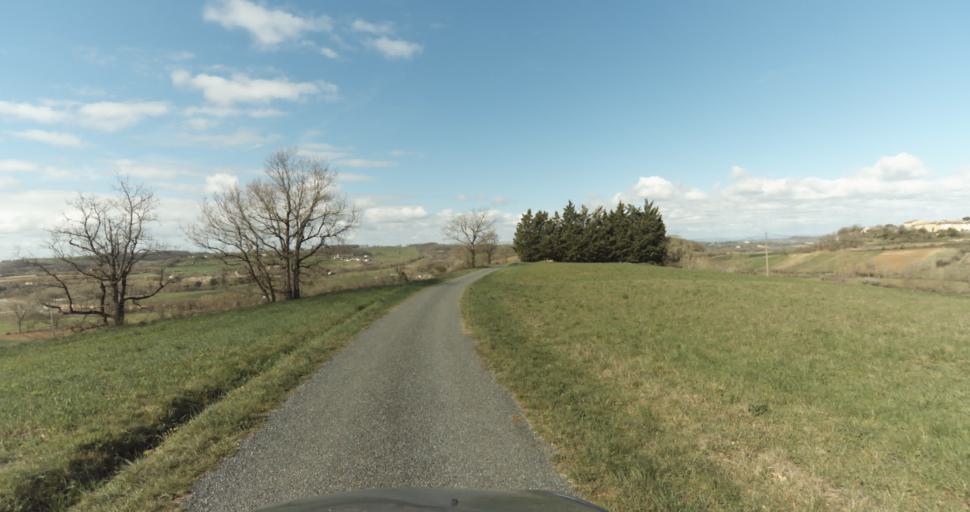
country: FR
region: Midi-Pyrenees
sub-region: Departement du Tarn
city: Frejairolles
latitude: 43.8614
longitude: 2.1963
